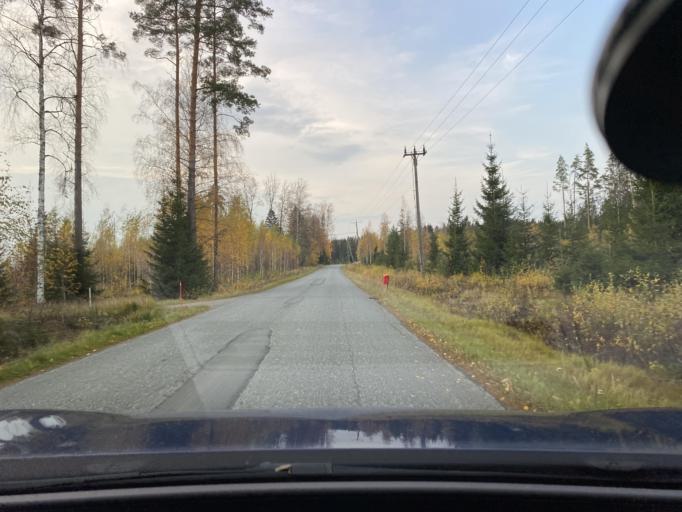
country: FI
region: Pirkanmaa
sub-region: Lounais-Pirkanmaa
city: Punkalaidun
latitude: 61.0710
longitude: 22.9721
